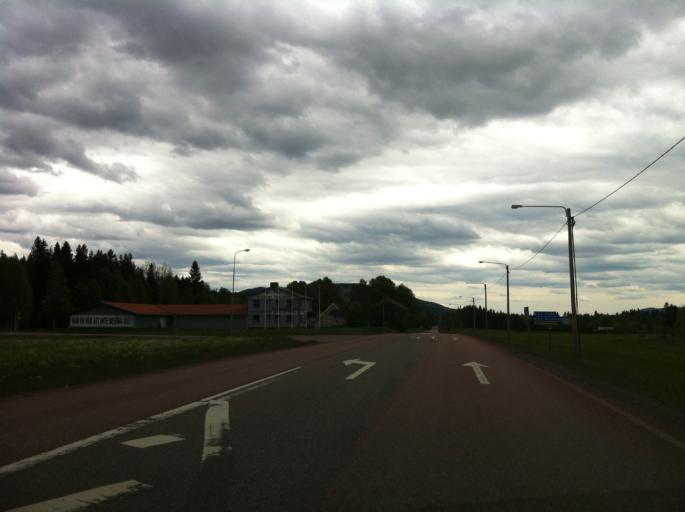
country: SE
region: Dalarna
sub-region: Malung-Saelens kommun
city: Malung
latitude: 61.0777
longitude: 13.3258
